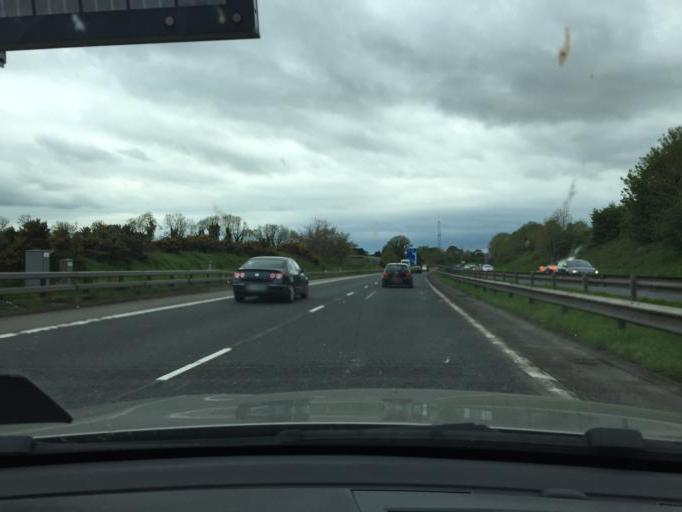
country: GB
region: Northern Ireland
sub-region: Lisburn District
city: Lisburn
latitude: 54.4989
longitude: -6.0395
